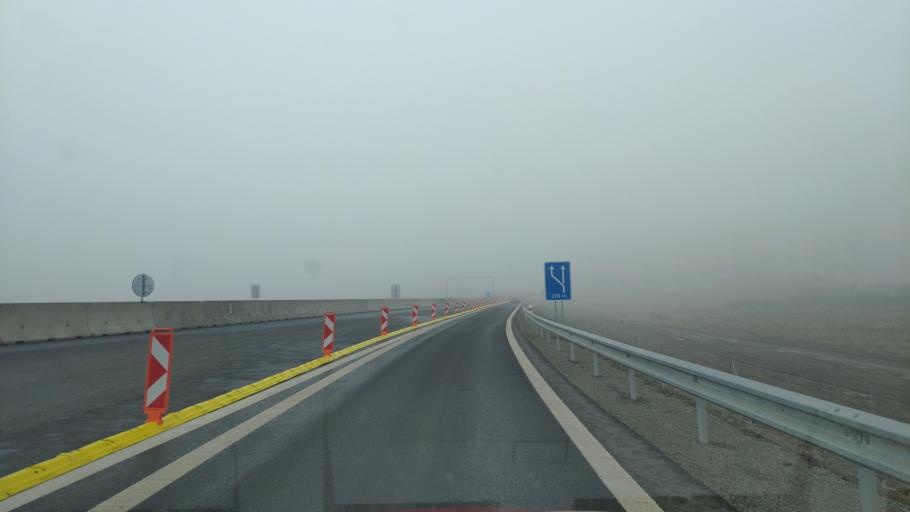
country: SK
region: Kosicky
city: Kosice
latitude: 48.7247
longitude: 21.4343
